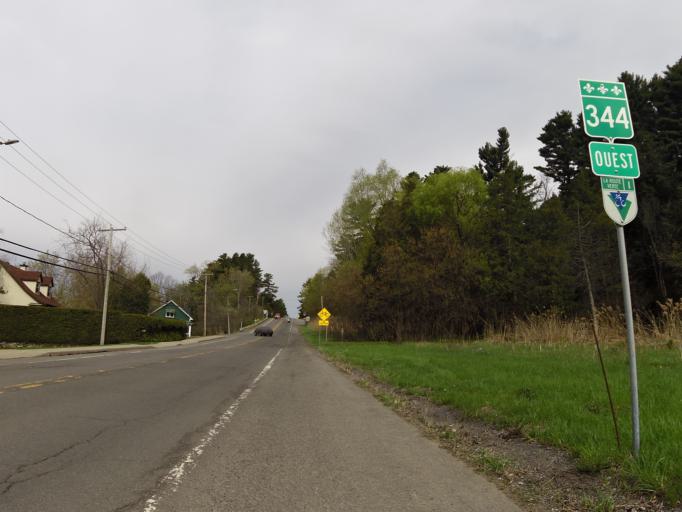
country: CA
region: Quebec
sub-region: Laurentides
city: Oka
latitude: 45.4627
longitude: -74.0965
